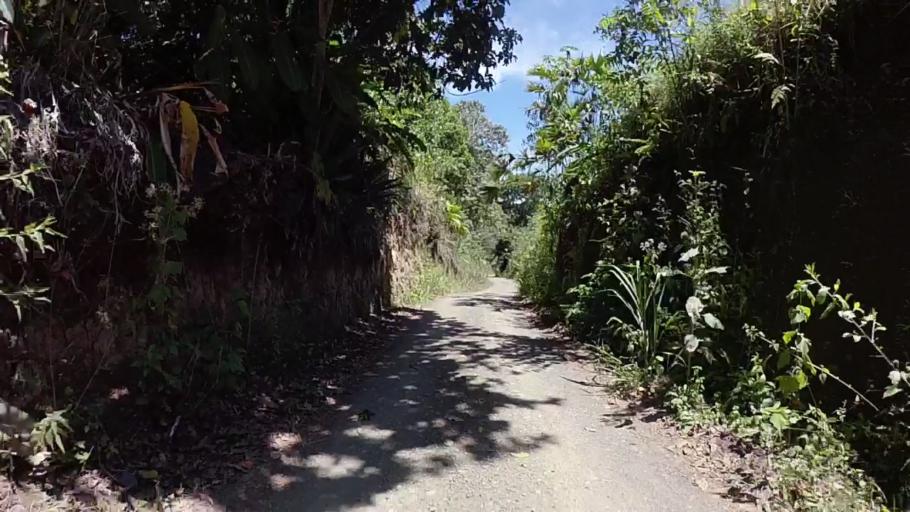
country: CO
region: Valle del Cauca
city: Alcala
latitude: 4.7046
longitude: -75.8246
